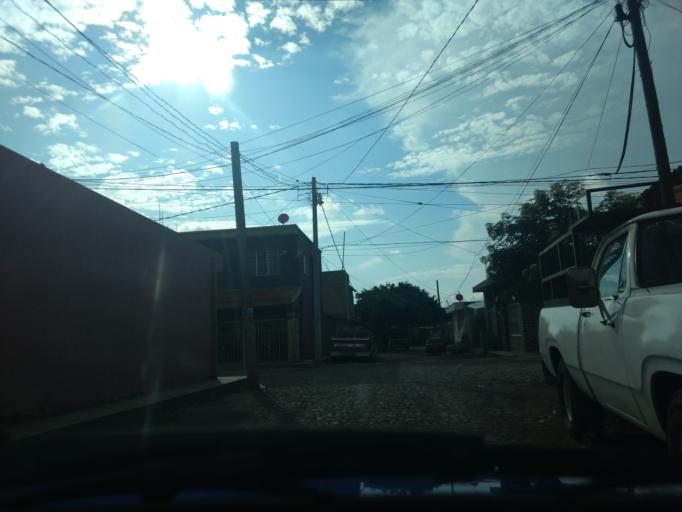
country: MX
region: Nayarit
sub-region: Tepic
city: La Corregidora
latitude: 21.4514
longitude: -104.8132
